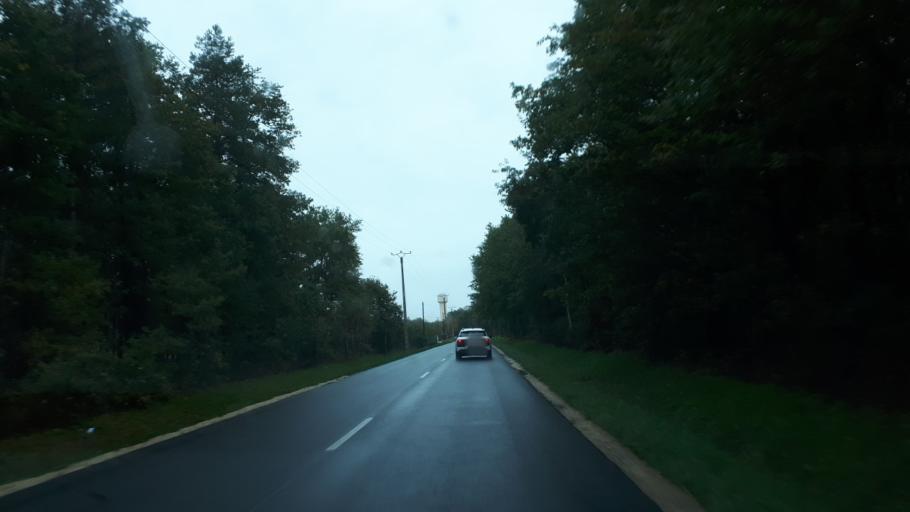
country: FR
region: Centre
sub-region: Departement du Loir-et-Cher
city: Gievres
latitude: 47.2921
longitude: 1.6708
